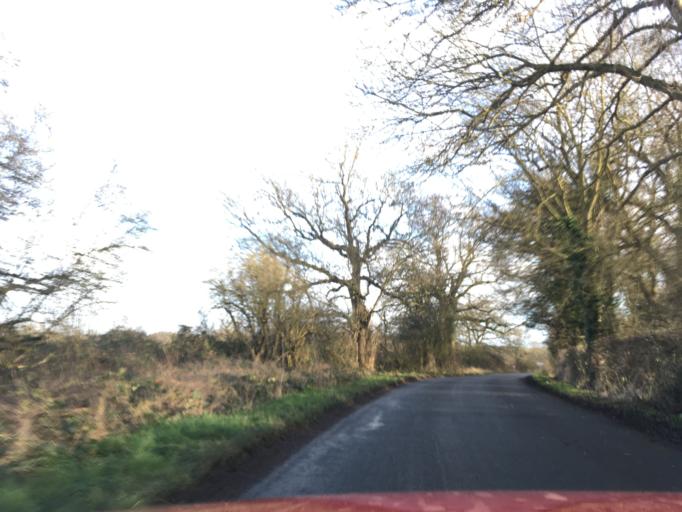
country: GB
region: England
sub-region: Warwickshire
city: Henley in Arden
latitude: 52.2216
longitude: -1.7880
